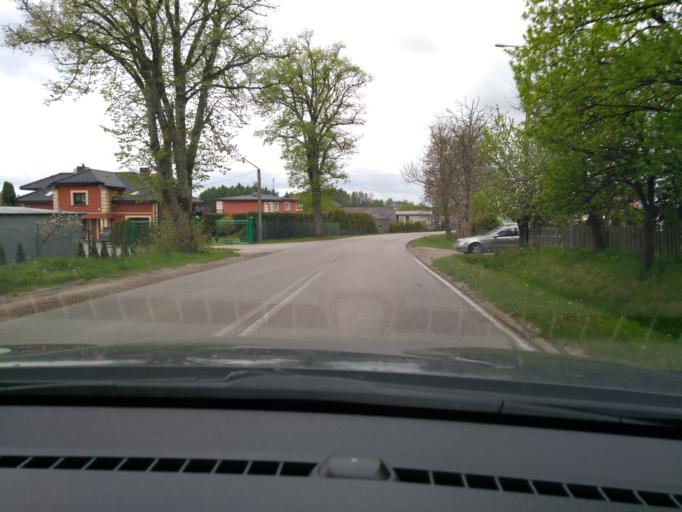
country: PL
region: Pomeranian Voivodeship
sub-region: Powiat kartuski
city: Sierakowice
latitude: 54.3411
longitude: 17.9285
